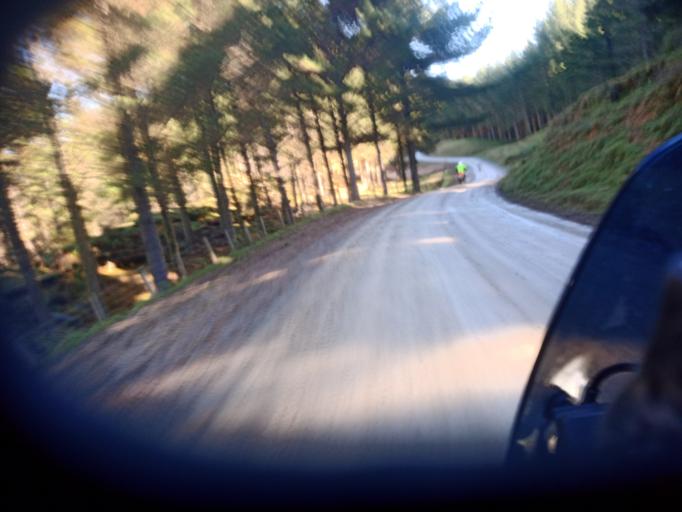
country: NZ
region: Gisborne
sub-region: Gisborne District
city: Gisborne
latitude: -38.1001
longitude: 178.1156
